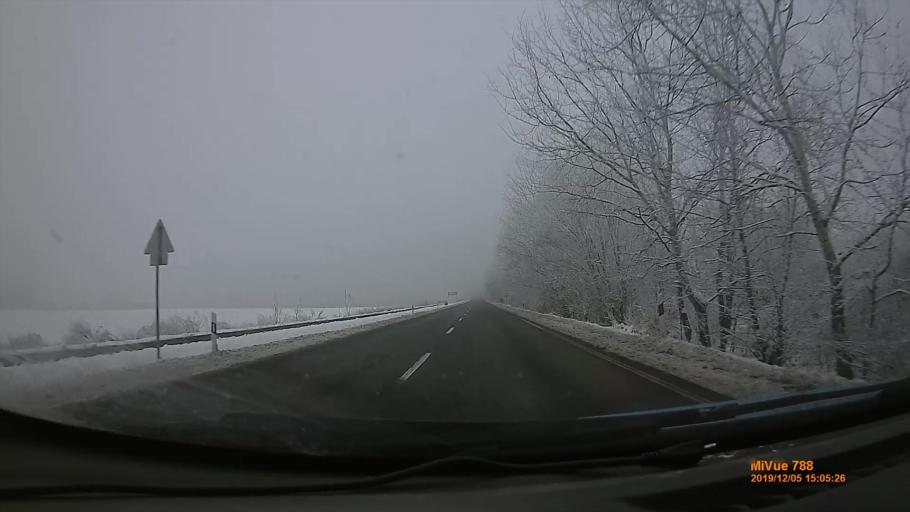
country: HU
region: Szabolcs-Szatmar-Bereg
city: Tiszanagyfalu
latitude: 48.1098
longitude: 21.4870
